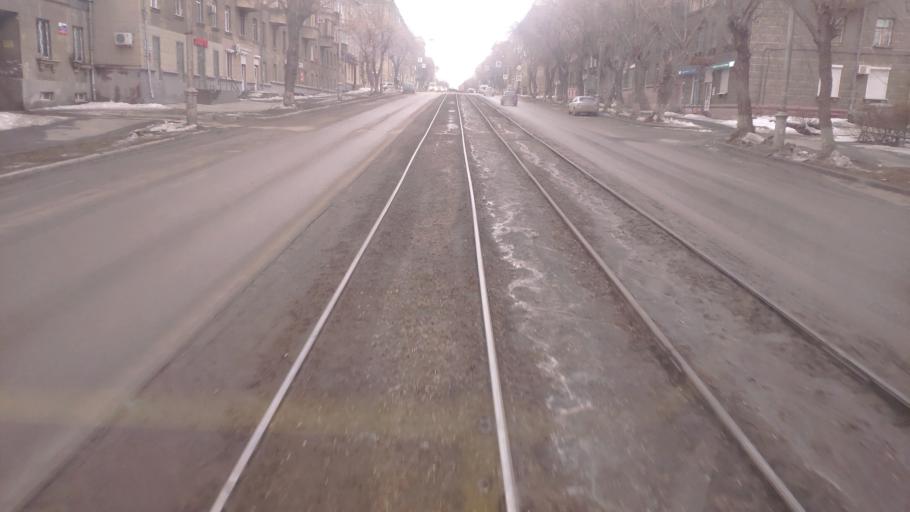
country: RU
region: Chelyabinsk
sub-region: Gorod Magnitogorsk
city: Magnitogorsk
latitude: 53.4204
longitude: 58.9996
